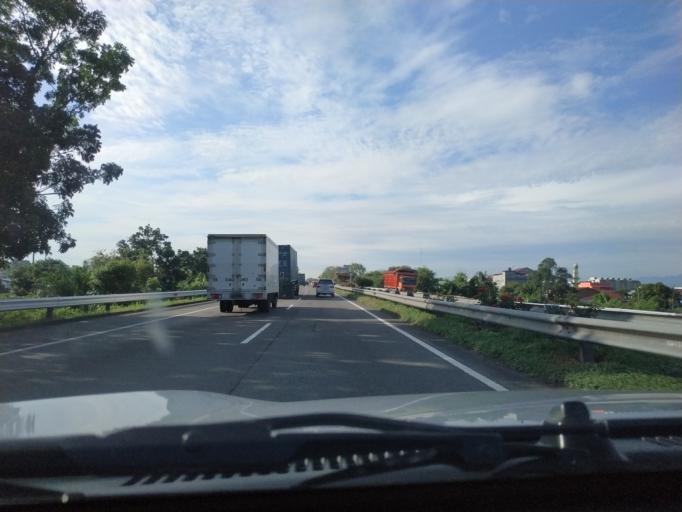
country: ID
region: North Sumatra
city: Medan
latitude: 3.5844
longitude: 98.7241
